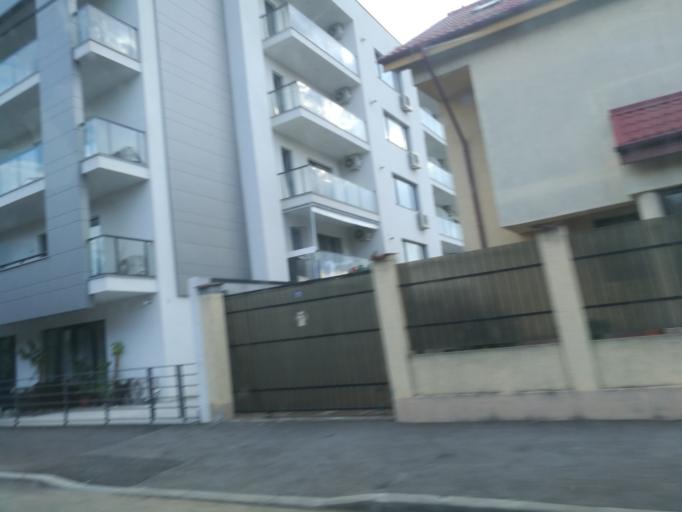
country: RO
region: Ilfov
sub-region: Comuna Otopeni
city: Otopeni
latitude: 44.4983
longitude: 26.0692
